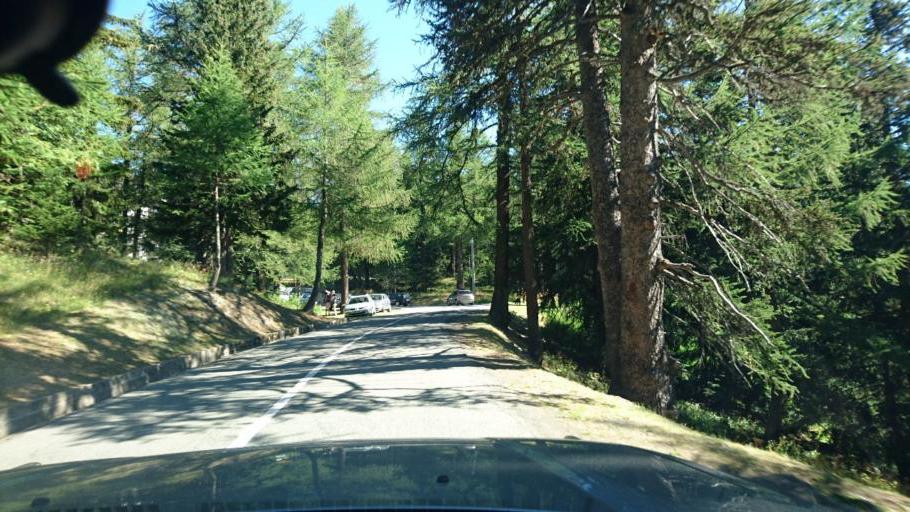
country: IT
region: Aosta Valley
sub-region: Valle d'Aosta
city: Pre Saint Didier
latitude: 45.7422
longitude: 6.9898
